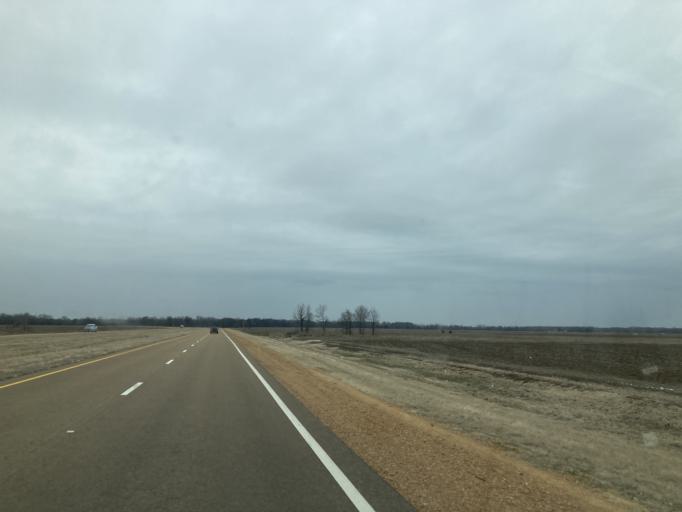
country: US
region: Mississippi
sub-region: Humphreys County
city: Belzoni
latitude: 33.0653
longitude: -90.4722
